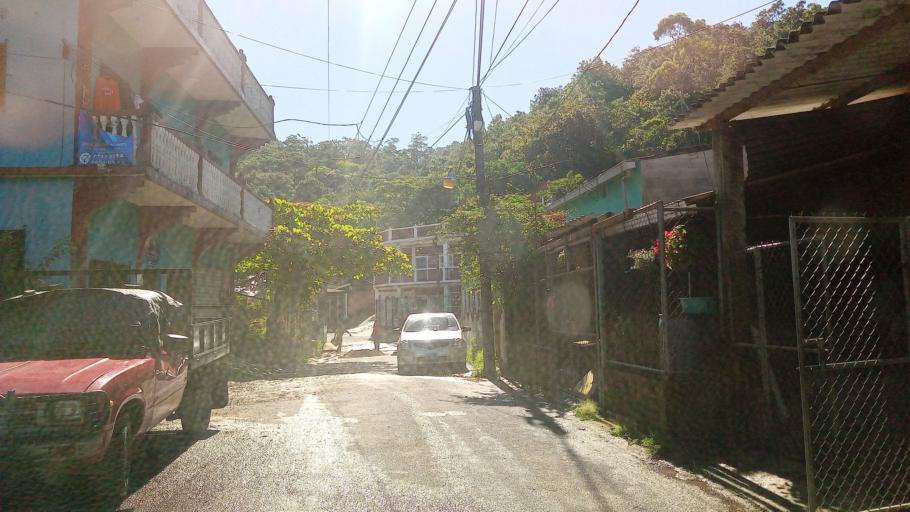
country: HN
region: Ocotepeque
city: Antigua Ocotepeque
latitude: 14.3126
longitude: -89.1613
